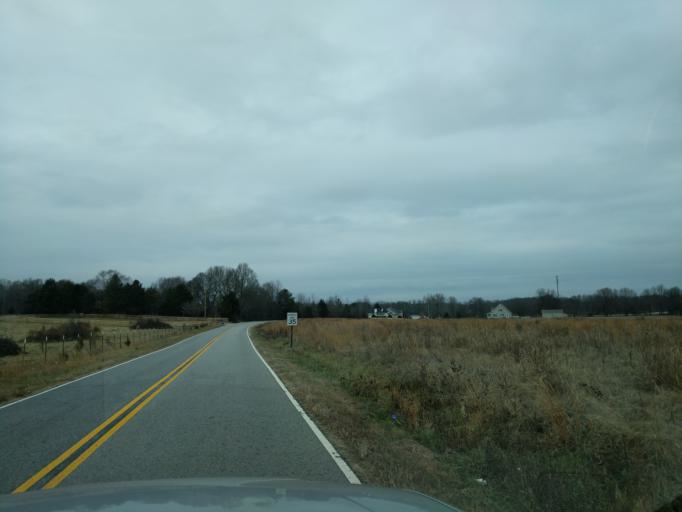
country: US
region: South Carolina
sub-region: Spartanburg County
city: Duncan
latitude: 34.8635
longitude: -82.1248
